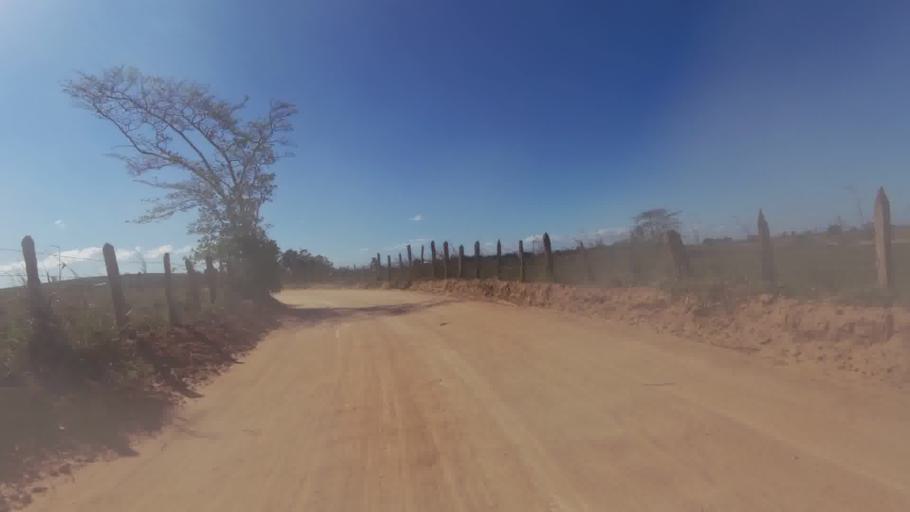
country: BR
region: Espirito Santo
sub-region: Marataizes
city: Marataizes
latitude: -21.1401
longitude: -40.9912
